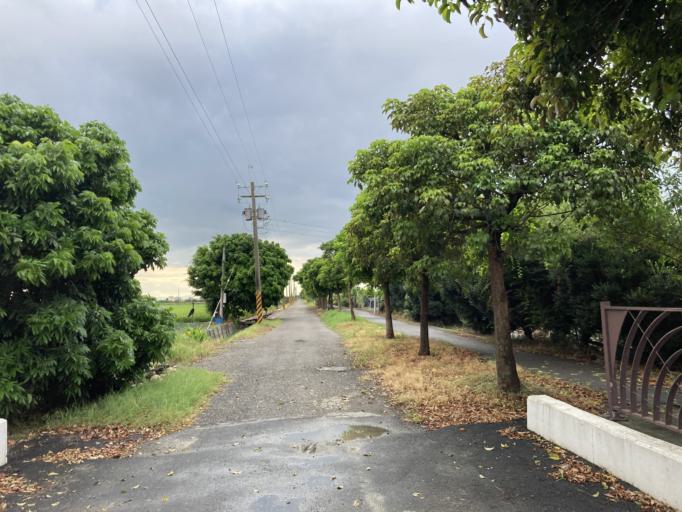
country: TW
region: Taiwan
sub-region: Yunlin
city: Douliu
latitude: 23.8789
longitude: 120.3632
